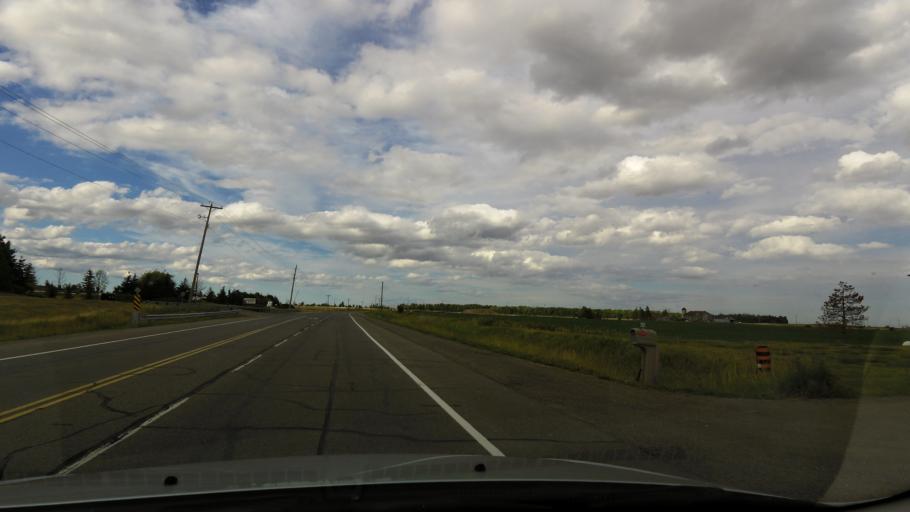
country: CA
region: Ontario
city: Brampton
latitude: 43.6902
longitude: -79.8717
